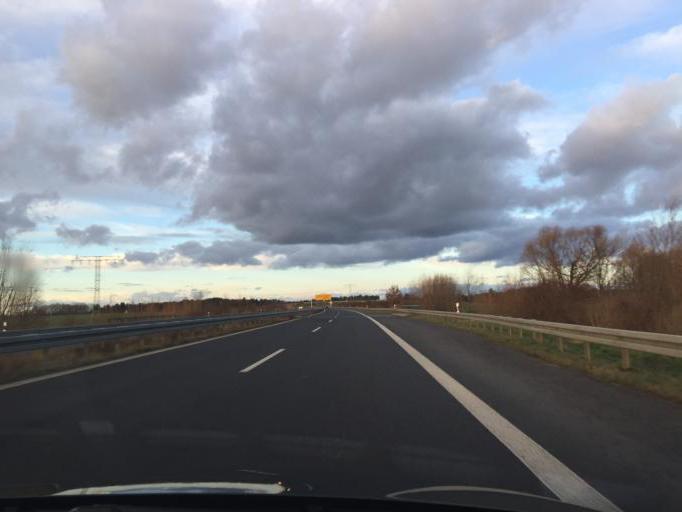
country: DE
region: Brandenburg
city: Rangsdorf
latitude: 52.3352
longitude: 13.4451
